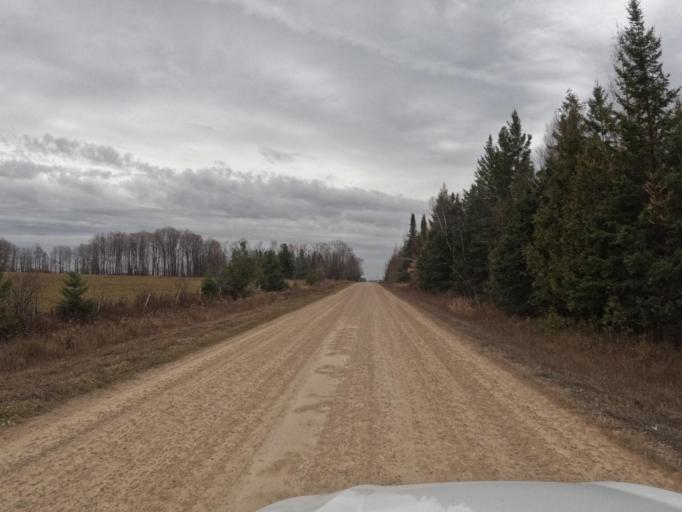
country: CA
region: Ontario
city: Shelburne
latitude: 44.0255
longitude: -80.3930
